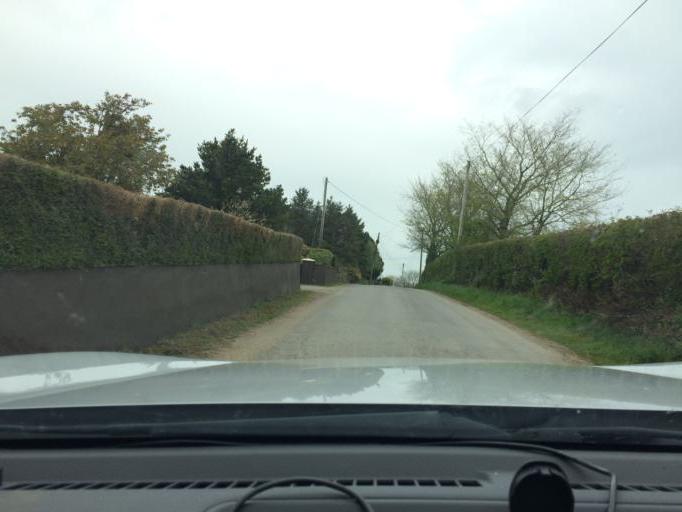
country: IE
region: Munster
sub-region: Waterford
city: Dungarvan
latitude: 52.0561
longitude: -7.6097
